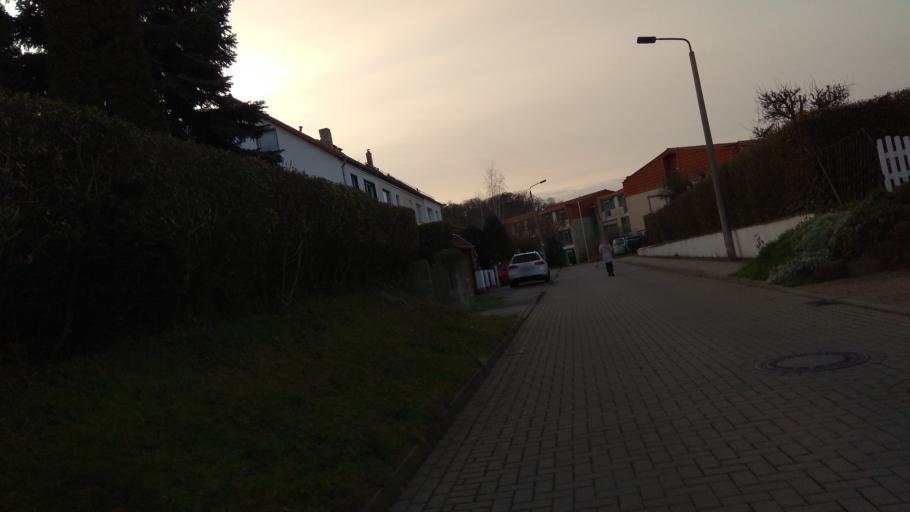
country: DE
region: Saxony-Anhalt
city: Halberstadt
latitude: 51.8742
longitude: 11.0513
